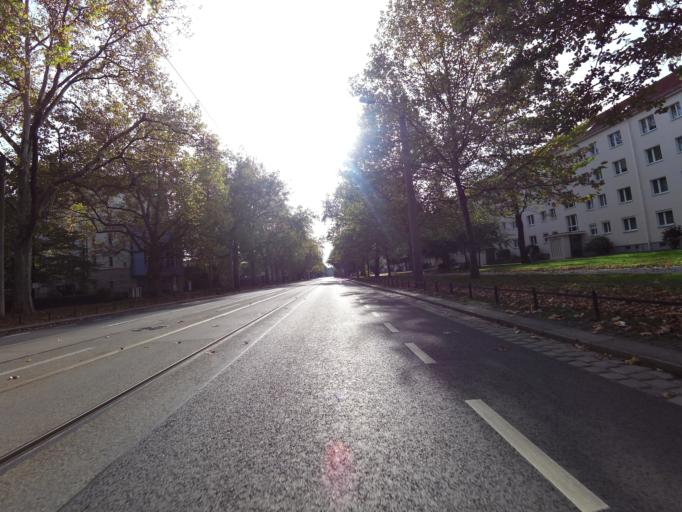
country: DE
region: Saxony
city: Dresden
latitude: 51.0443
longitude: 13.7692
